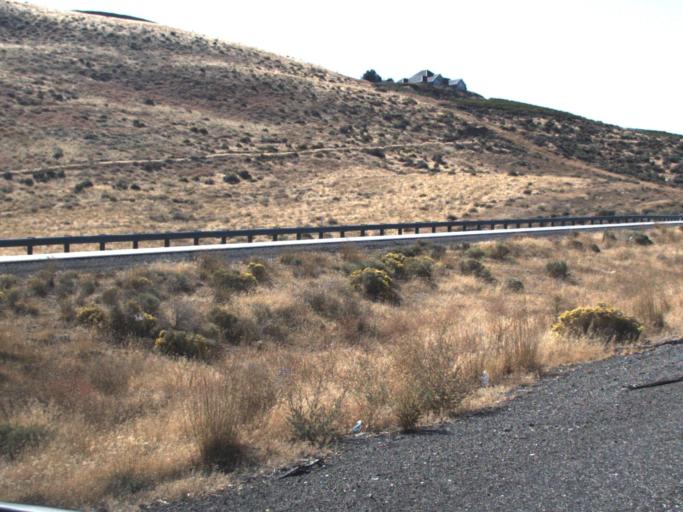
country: US
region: Washington
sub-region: Benton County
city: West Richland
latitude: 46.2467
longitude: -119.3359
